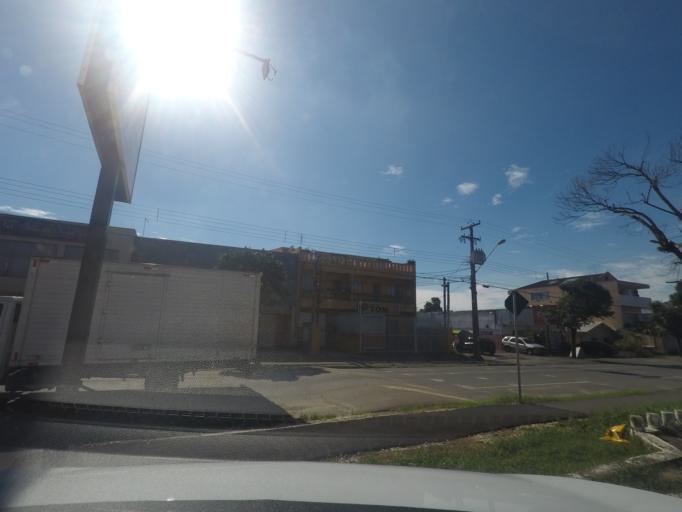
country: BR
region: Parana
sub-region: Sao Jose Dos Pinhais
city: Sao Jose dos Pinhais
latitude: -25.5100
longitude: -49.2778
